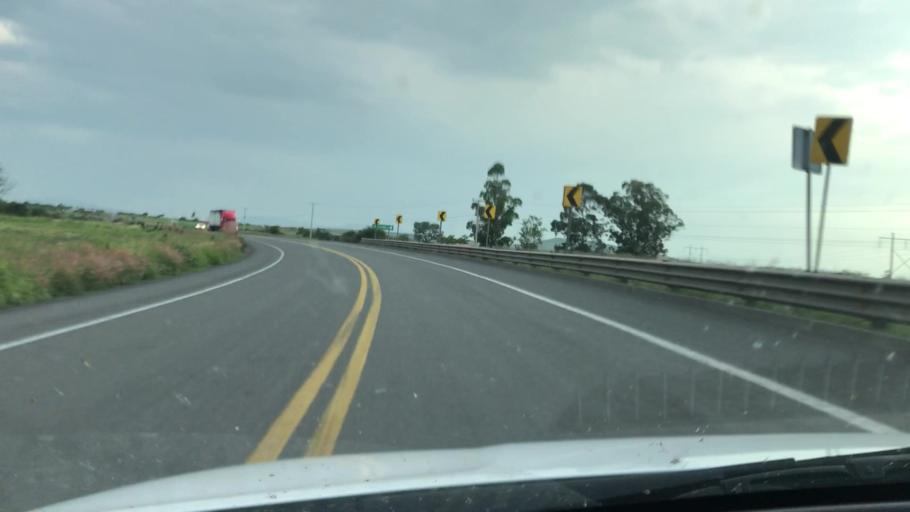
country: MX
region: Jalisco
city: Degollado
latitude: 20.3609
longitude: -102.1485
